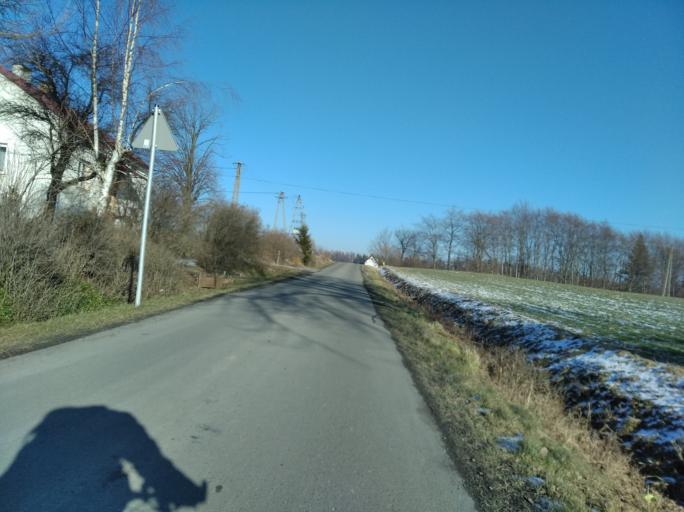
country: PL
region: Subcarpathian Voivodeship
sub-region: Powiat strzyzowski
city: Konieczkowa
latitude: 49.8586
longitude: 21.9581
